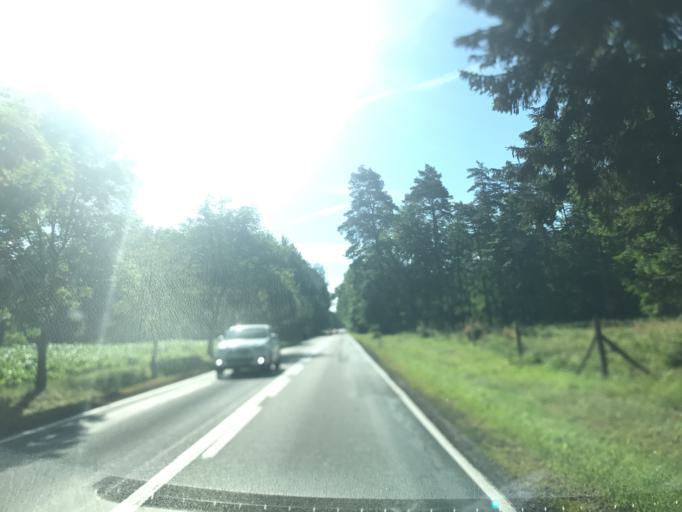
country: PL
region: Pomeranian Voivodeship
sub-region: Powiat czluchowski
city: Czluchow
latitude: 53.7026
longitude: 17.2740
